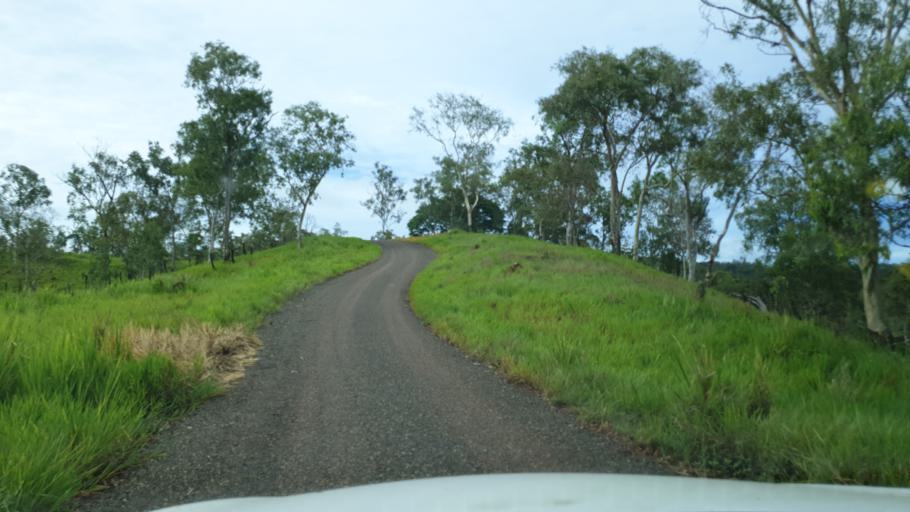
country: PG
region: National Capital
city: Port Moresby
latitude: -9.4309
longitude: 147.3941
